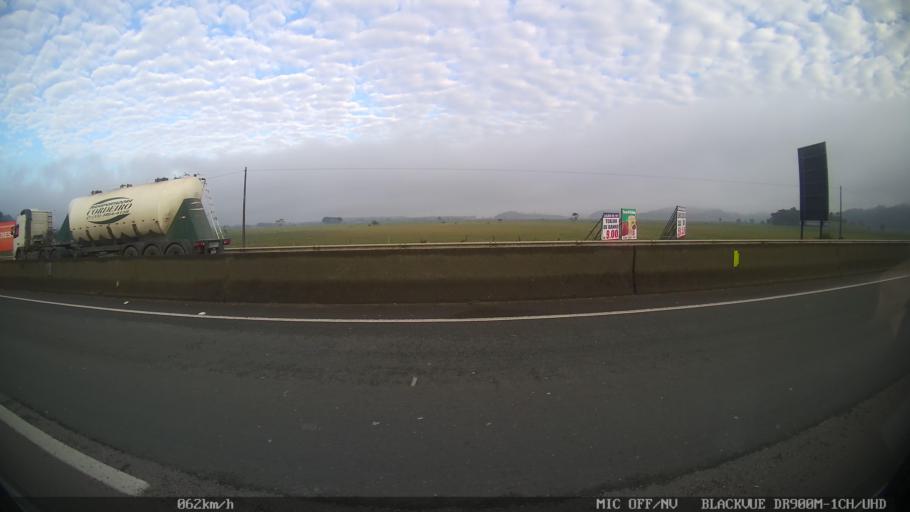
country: BR
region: Santa Catarina
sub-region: Penha
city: Penha
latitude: -26.8173
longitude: -48.6833
